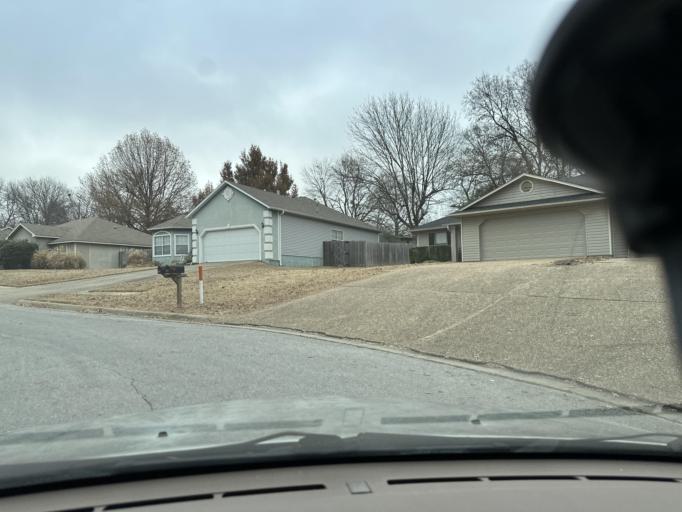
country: US
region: Arkansas
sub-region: Washington County
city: Fayetteville
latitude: 36.0840
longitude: -94.1175
